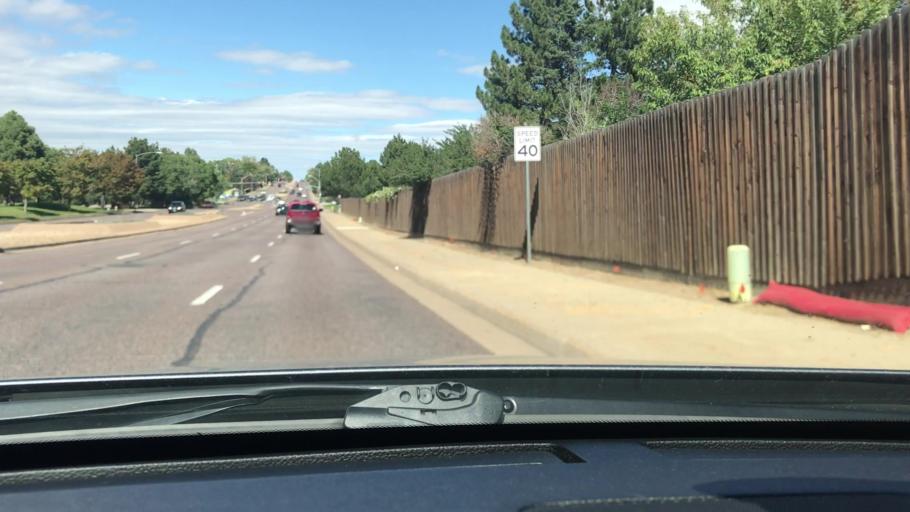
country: US
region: Colorado
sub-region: Arapahoe County
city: Dove Valley
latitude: 39.6300
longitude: -104.8102
